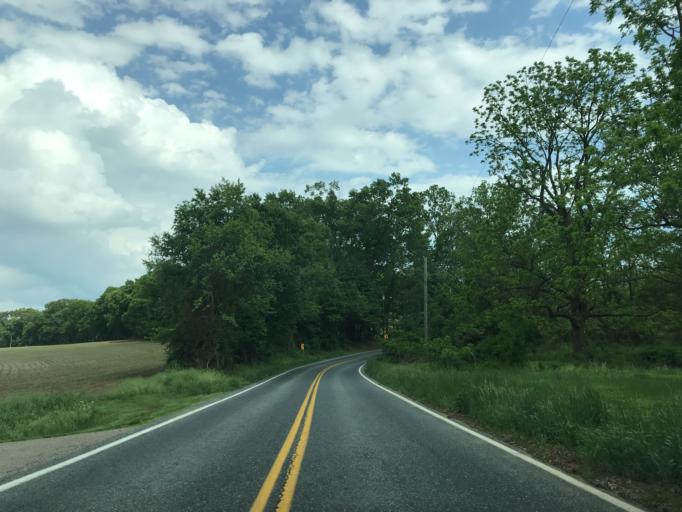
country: US
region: Pennsylvania
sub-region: York County
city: Susquehanna Trails
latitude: 39.6743
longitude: -76.3842
